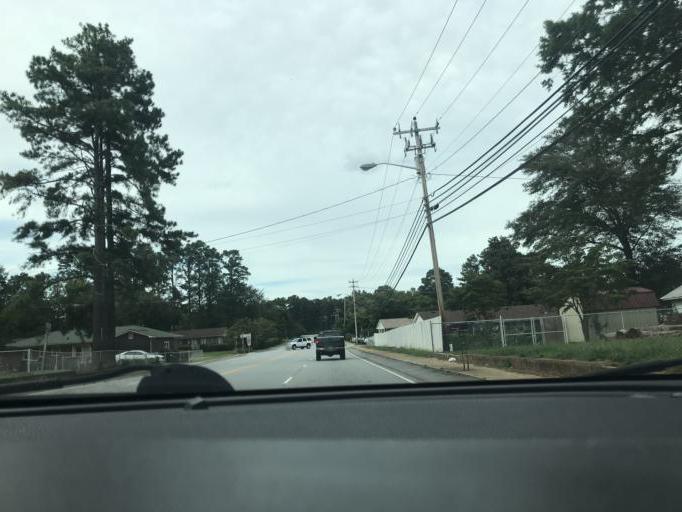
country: US
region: South Carolina
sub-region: Cherokee County
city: Gaffney
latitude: 35.0930
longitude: -81.6607
